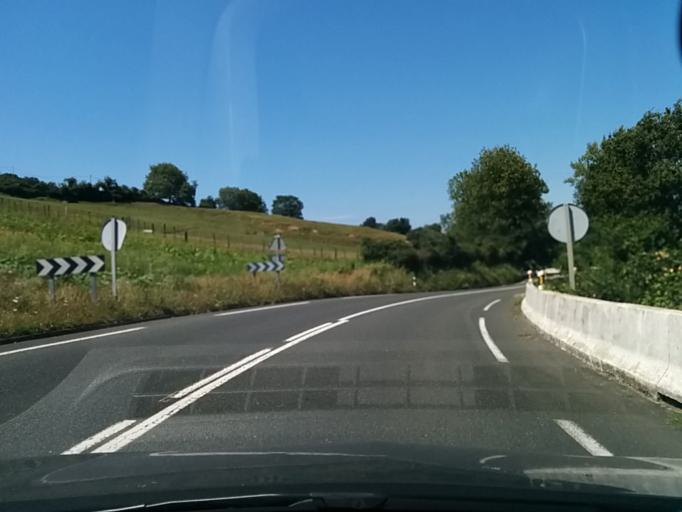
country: ES
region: Basque Country
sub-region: Provincia de Guipuzcoa
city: Deba
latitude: 43.2876
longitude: -2.3395
